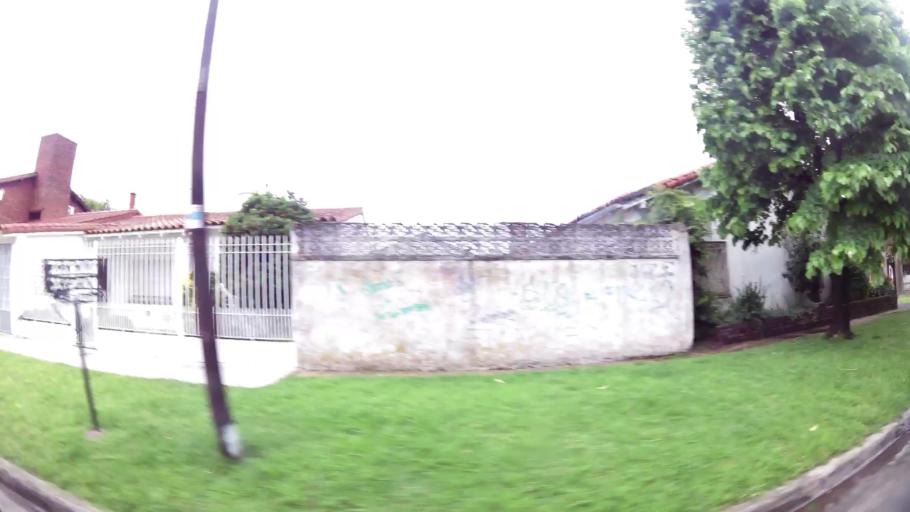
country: AR
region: Buenos Aires
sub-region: Partido de Lomas de Zamora
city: Lomas de Zamora
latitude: -34.7488
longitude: -58.3723
